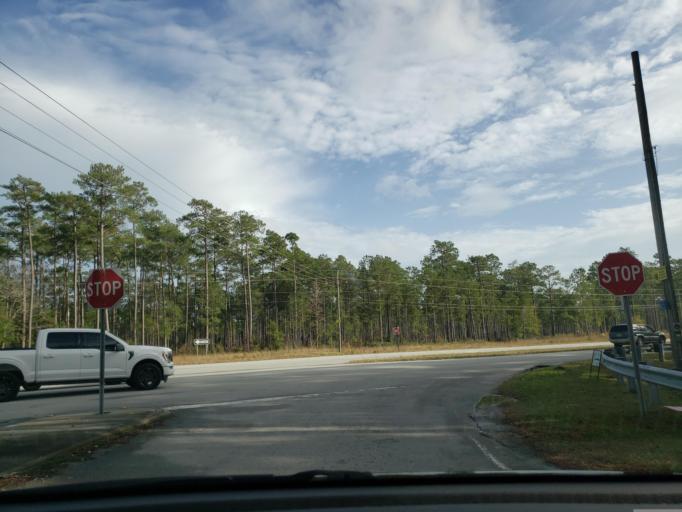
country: US
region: North Carolina
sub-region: Onslow County
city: Jacksonville
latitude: 34.6545
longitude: -77.4758
